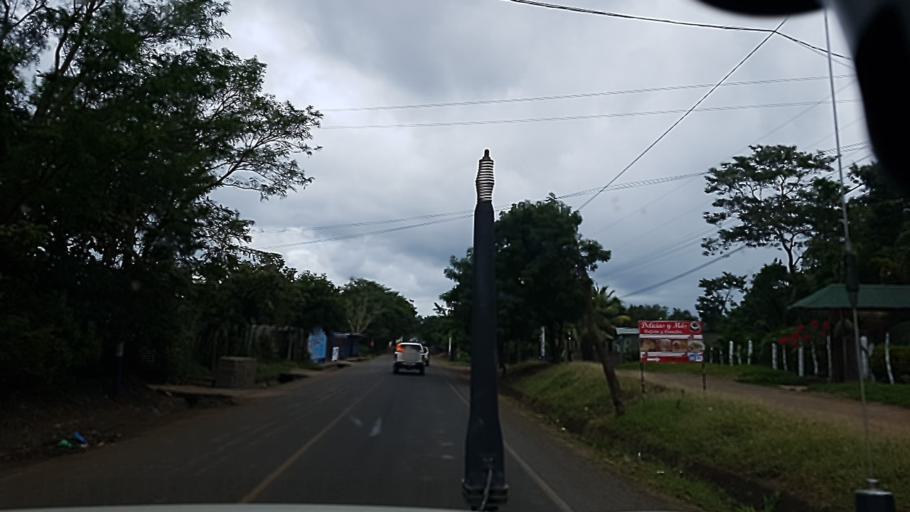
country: NI
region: Carazo
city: La Paz de Oriente
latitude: 11.8204
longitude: -86.1321
